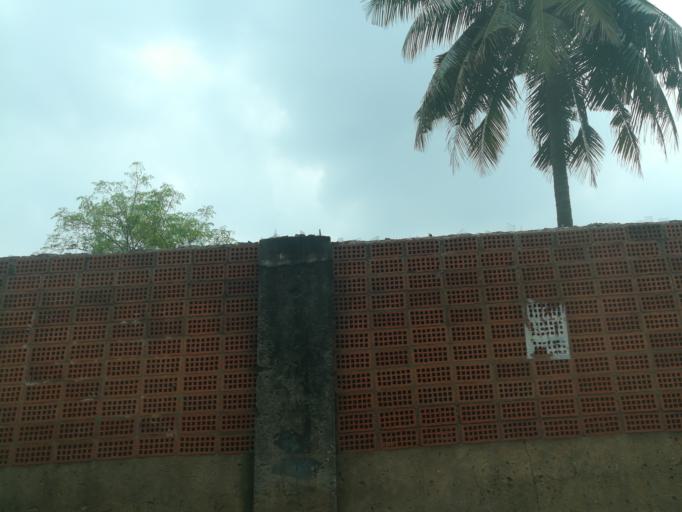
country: NG
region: Lagos
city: Ikorodu
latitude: 6.6198
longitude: 3.5189
